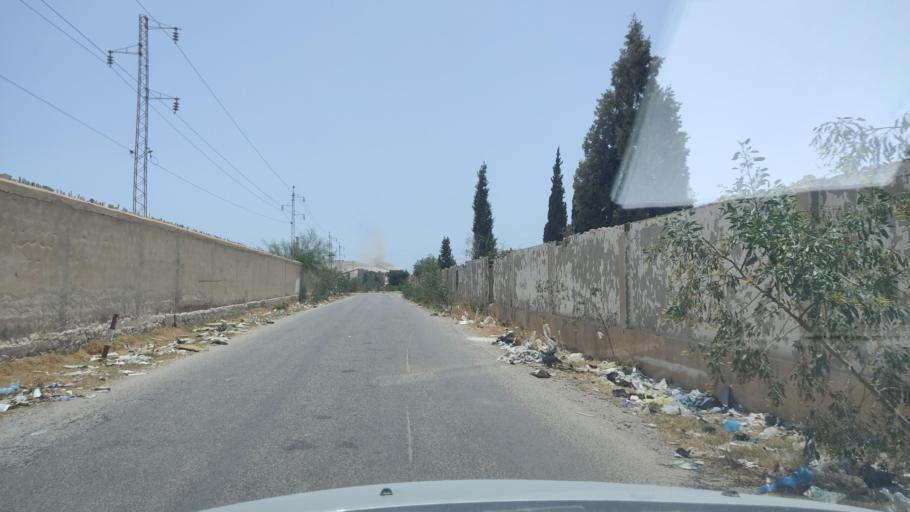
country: TN
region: Safaqis
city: Sfax
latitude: 34.7060
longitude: 10.7149
